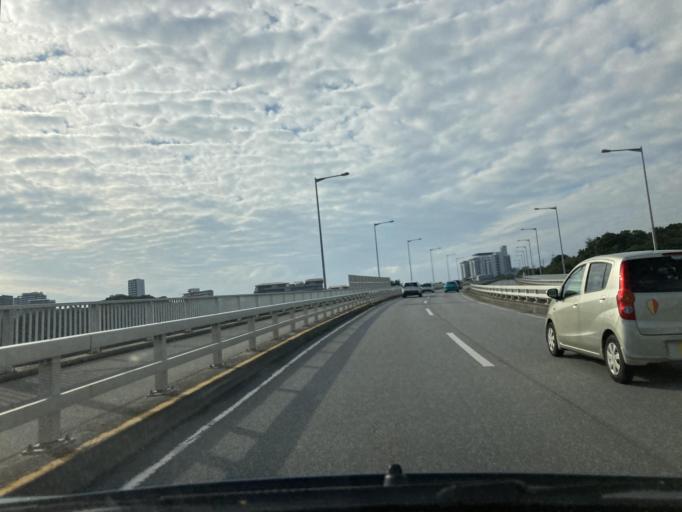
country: JP
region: Okinawa
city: Okinawa
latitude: 26.3145
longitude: 127.8054
